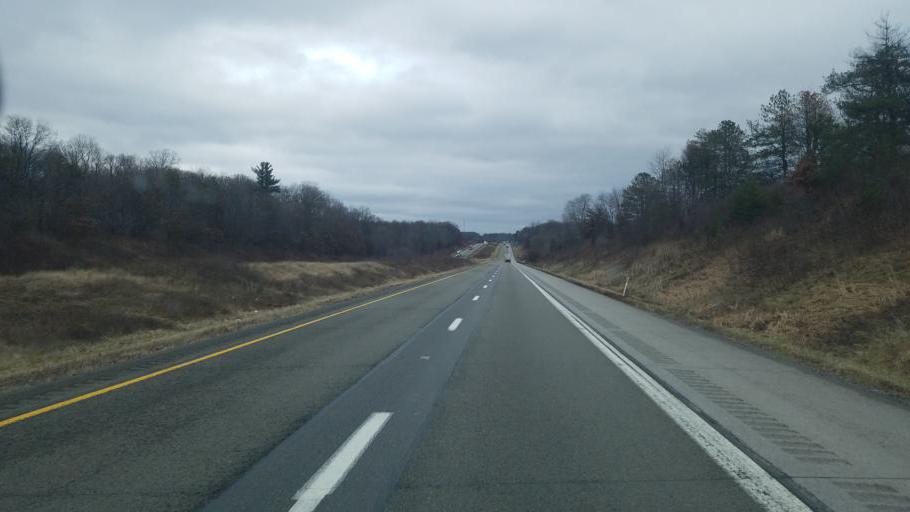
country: US
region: Pennsylvania
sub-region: Venango County
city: Seneca
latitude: 41.1857
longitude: -79.7904
